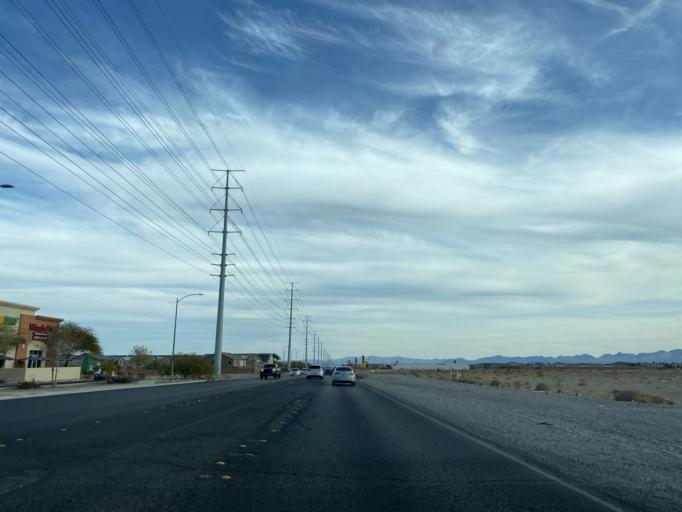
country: US
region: Nevada
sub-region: Clark County
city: Enterprise
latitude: 36.0555
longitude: -115.2688
